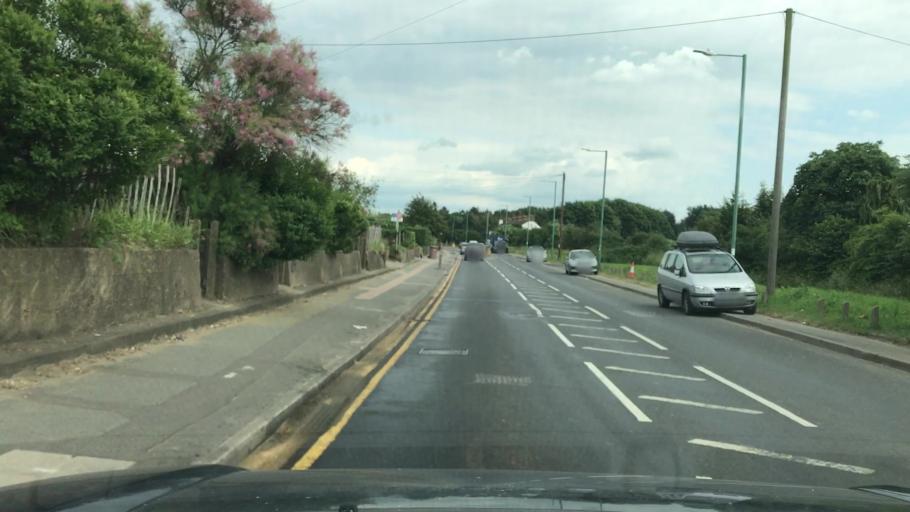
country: GB
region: England
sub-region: Kent
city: Stone
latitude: 51.4180
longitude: 0.2566
